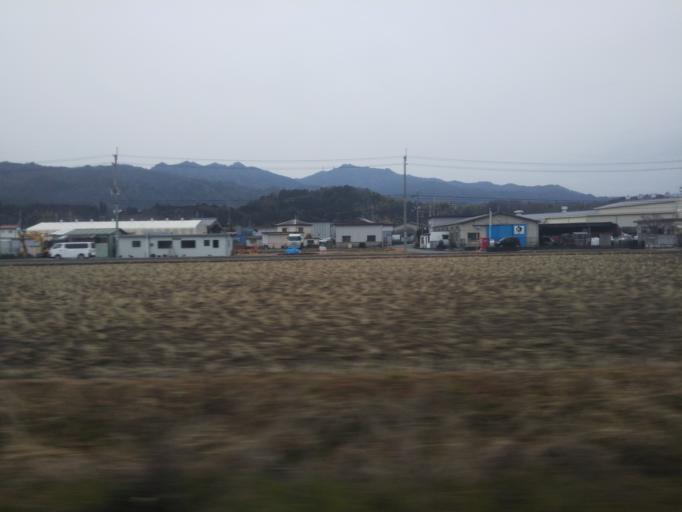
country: JP
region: Shiga Prefecture
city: Minakuchicho-matoba
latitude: 34.9964
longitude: 136.0896
